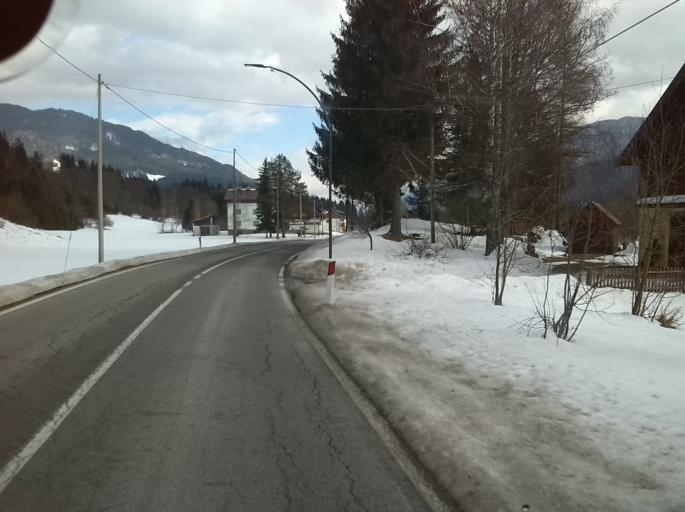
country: AT
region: Carinthia
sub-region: Politischer Bezirk Villach Land
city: Arnoldstein
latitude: 46.4992
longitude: 13.6876
